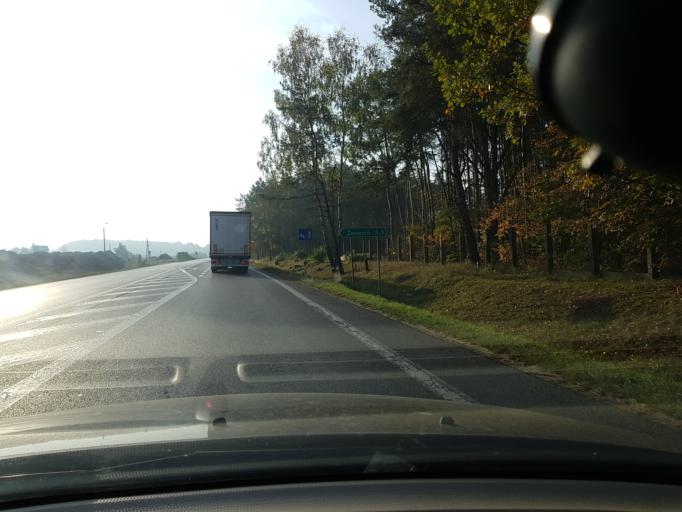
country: PL
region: Masovian Voivodeship
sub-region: Powiat otwocki
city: Otwock
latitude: 52.1527
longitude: 21.3143
